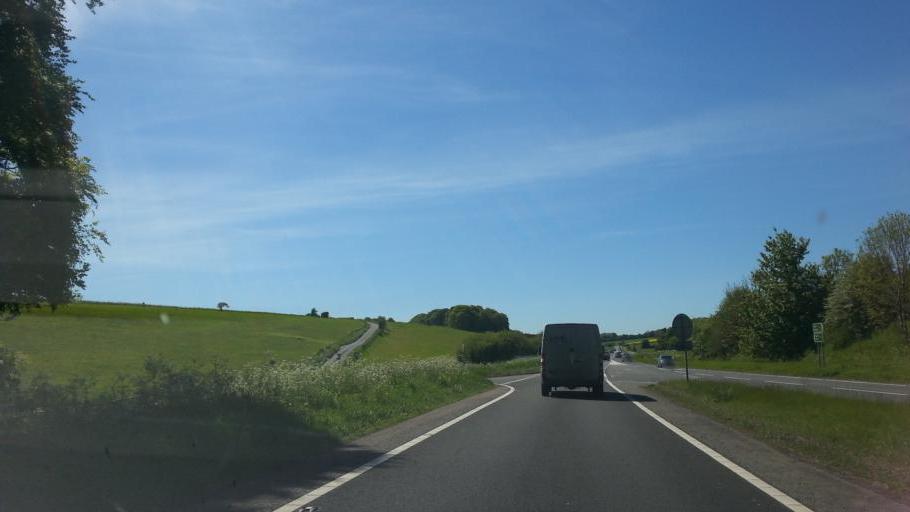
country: GB
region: England
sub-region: Wiltshire
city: Chicklade
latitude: 51.1083
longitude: -2.0955
